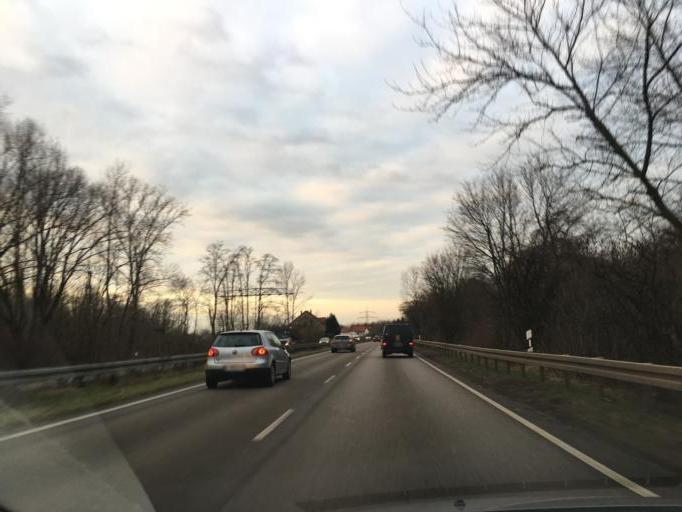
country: DE
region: Saxony
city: Espenhain
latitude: 51.1855
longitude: 12.4796
